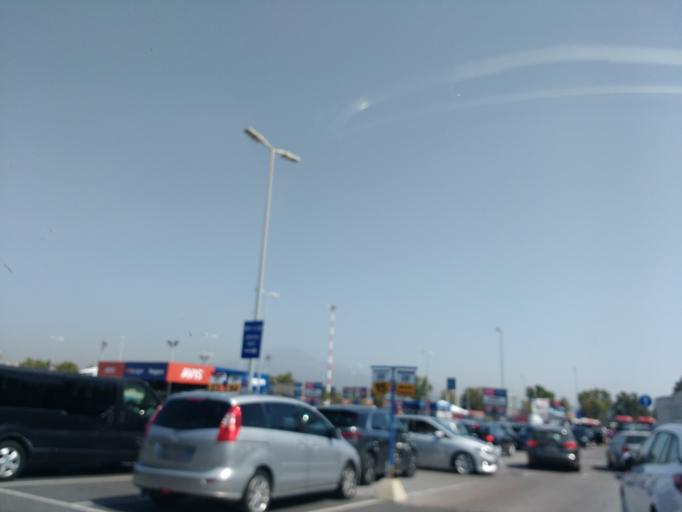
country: IT
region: Sicily
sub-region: Catania
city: Catania
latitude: 37.4713
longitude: 15.0707
